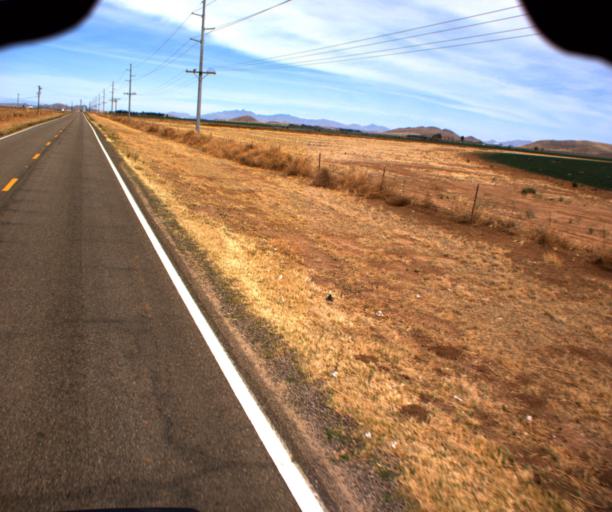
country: US
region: Arizona
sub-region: Cochise County
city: Tombstone
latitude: 31.8068
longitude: -109.6939
